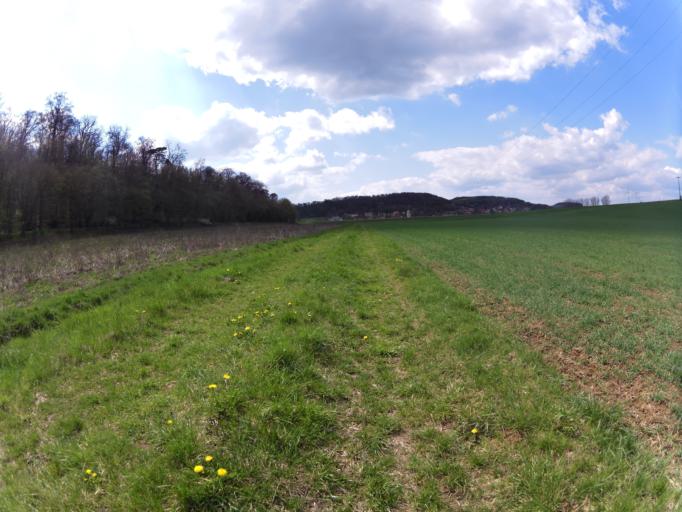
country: DE
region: Bavaria
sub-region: Regierungsbezirk Unterfranken
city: Greussenheim
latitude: 49.7936
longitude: 9.7694
